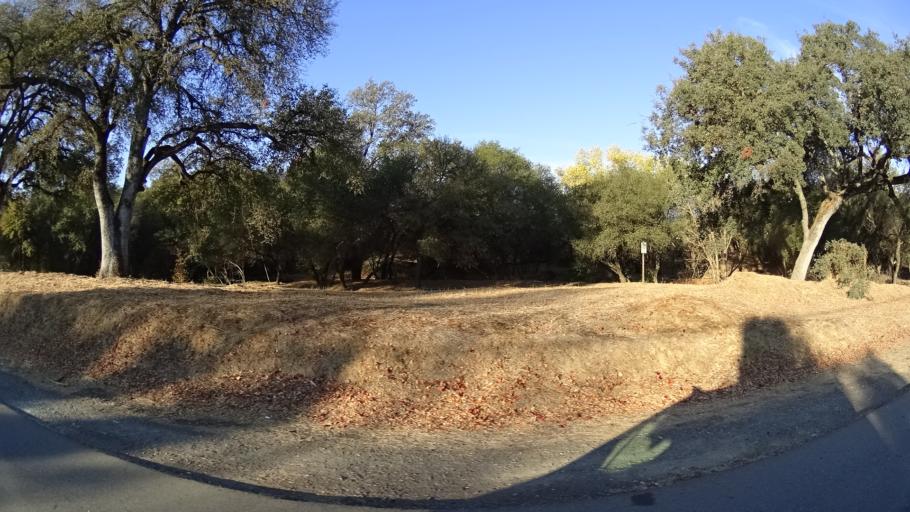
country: US
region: California
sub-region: Sacramento County
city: Antelope
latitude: 38.6971
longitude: -121.3087
